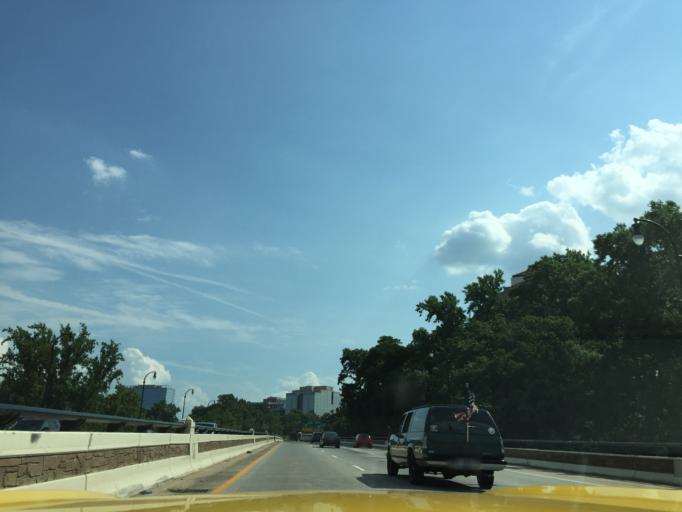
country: US
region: Delaware
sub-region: New Castle County
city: Wilmington
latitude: 39.7564
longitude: -75.5526
